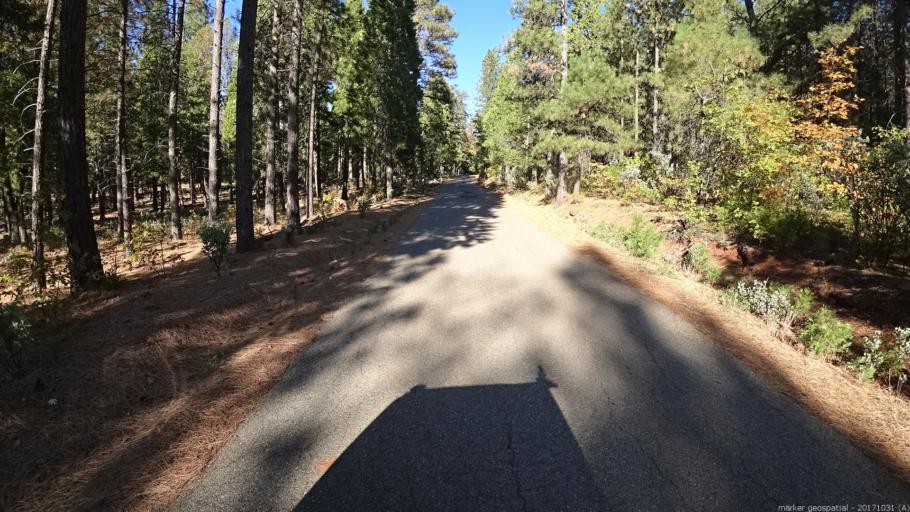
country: US
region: California
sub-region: Shasta County
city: Shingletown
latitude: 40.4866
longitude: -121.9269
